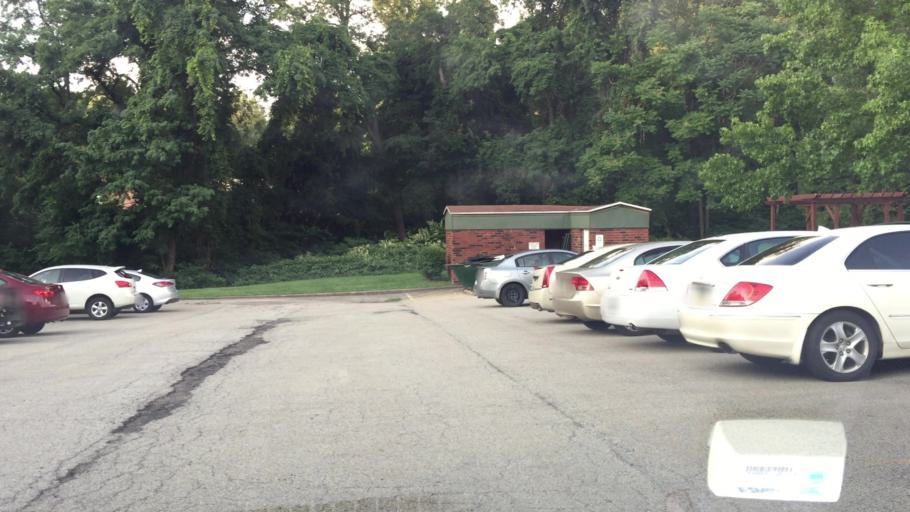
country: US
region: Pennsylvania
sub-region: Allegheny County
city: Swissvale
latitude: 40.4253
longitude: -79.8751
